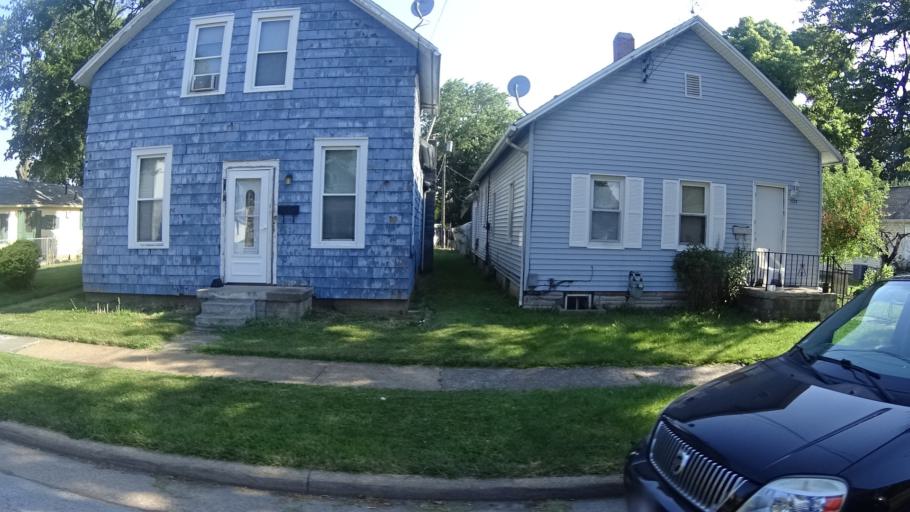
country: US
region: Ohio
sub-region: Erie County
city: Sandusky
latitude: 41.4510
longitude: -82.6948
